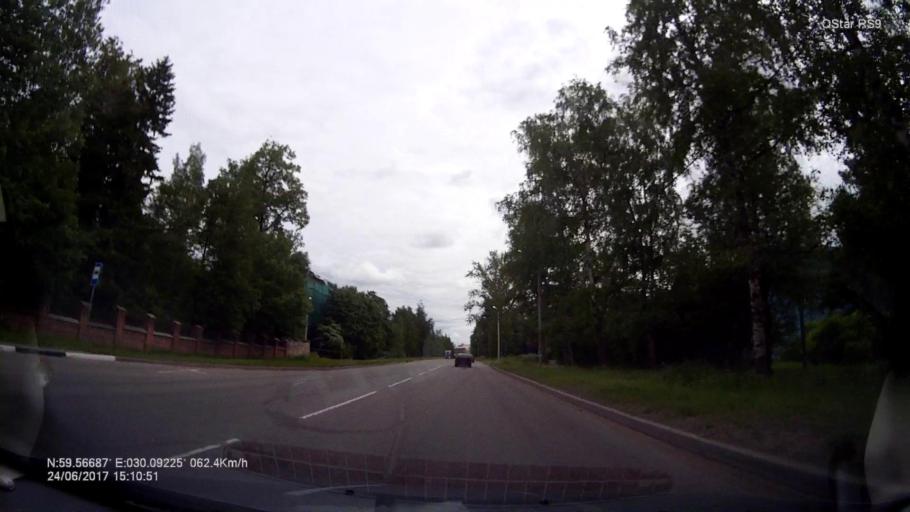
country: RU
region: Leningrad
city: Mariyenburg
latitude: 59.5667
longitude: 30.0927
